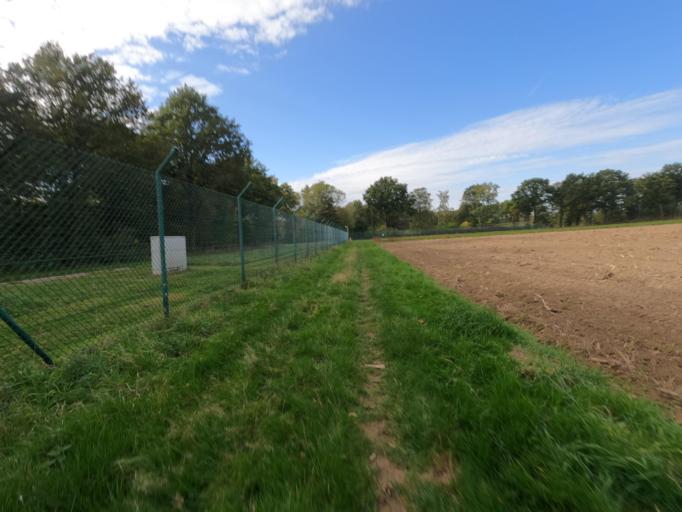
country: DE
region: North Rhine-Westphalia
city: Geilenkirchen
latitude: 50.9662
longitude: 6.0585
